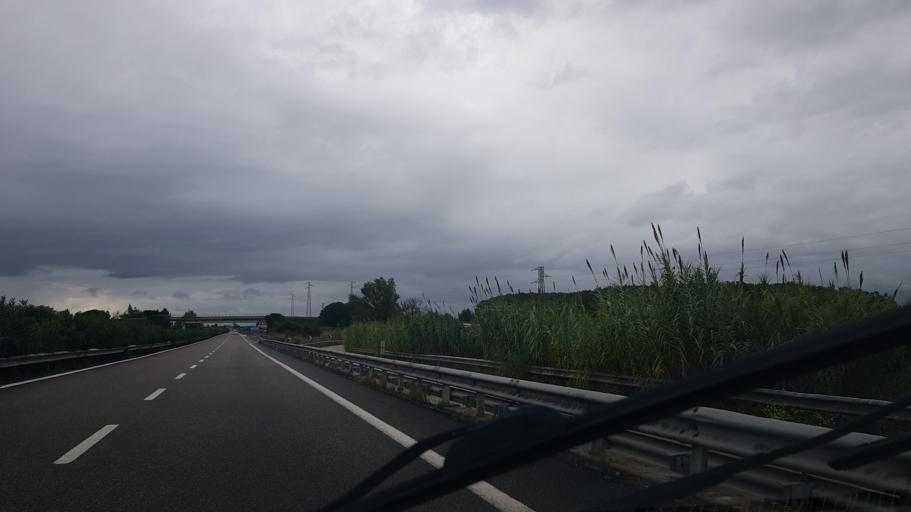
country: IT
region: Apulia
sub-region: Provincia di Taranto
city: Marina di Ginosa
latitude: 40.4356
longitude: 16.8376
